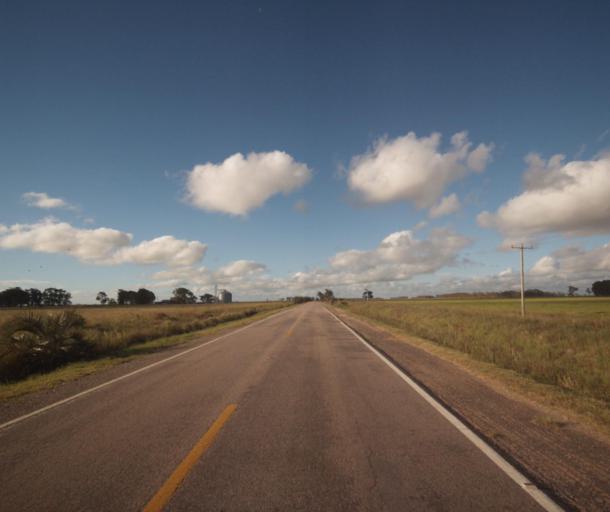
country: BR
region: Rio Grande do Sul
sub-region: Arroio Grande
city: Arroio Grande
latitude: -32.4483
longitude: -52.5699
